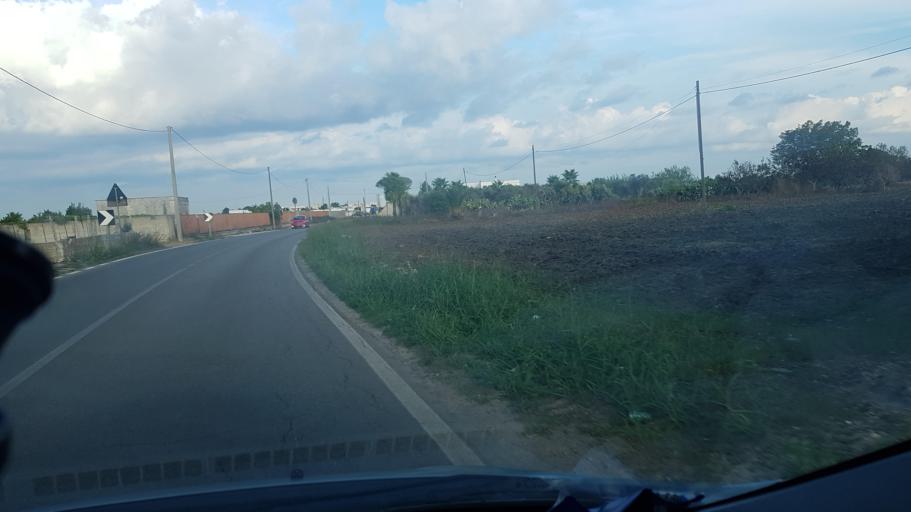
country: IT
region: Apulia
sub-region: Provincia di Lecce
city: Carmiano
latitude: 40.3456
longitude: 18.0270
